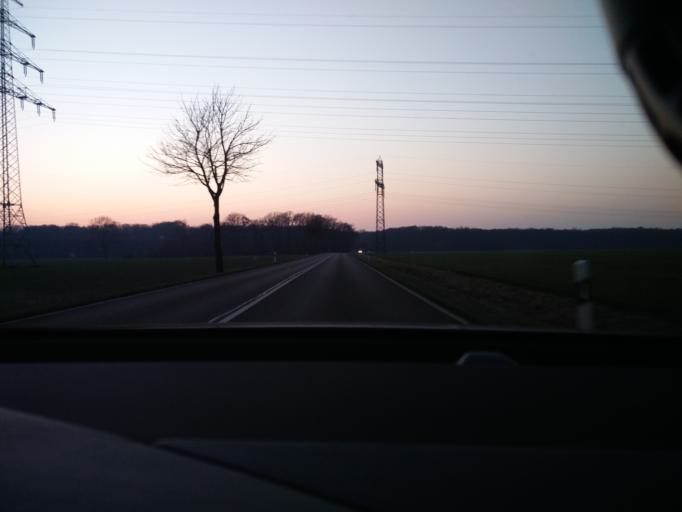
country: DE
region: Lower Saxony
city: Sehnde
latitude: 52.3143
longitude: 9.9053
